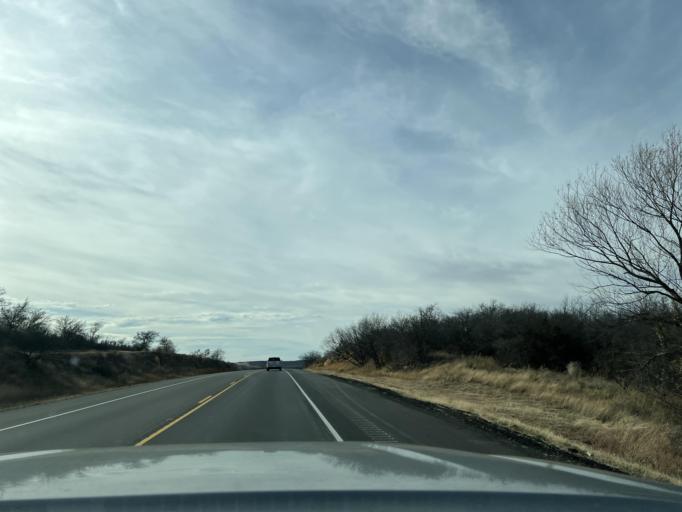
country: US
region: Texas
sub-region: Shackelford County
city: Albany
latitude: 32.7148
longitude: -99.3313
